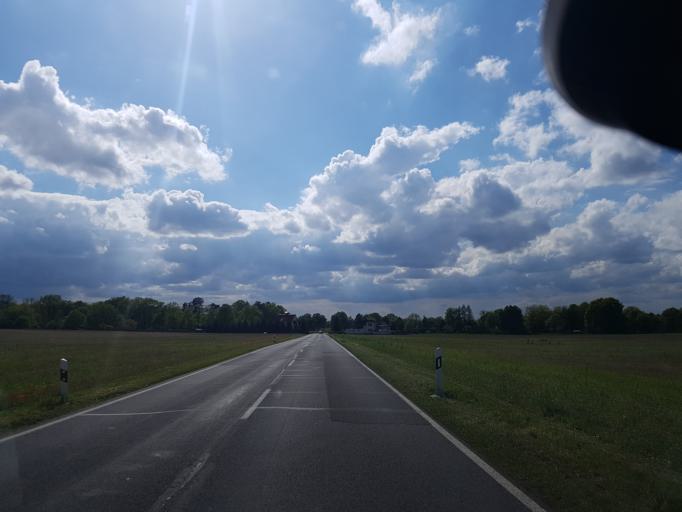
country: DE
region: Brandenburg
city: Drebkau
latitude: 51.6367
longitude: 14.2637
